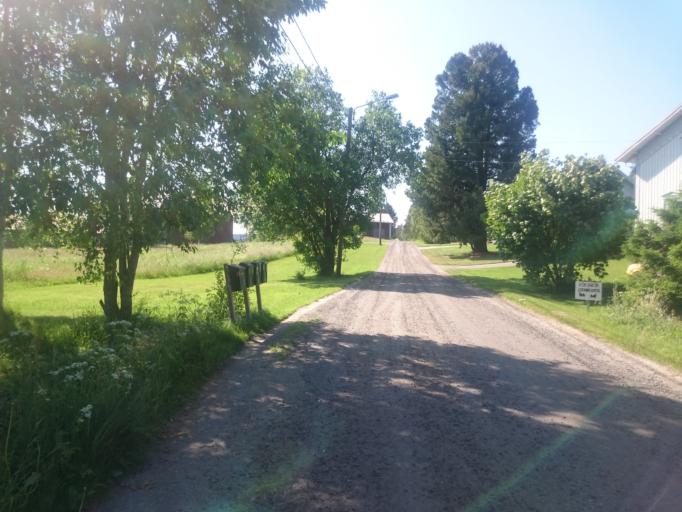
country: SE
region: Vaesternorrland
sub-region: OErnskoeldsviks Kommun
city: Bredbyn
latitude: 63.3000
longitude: 18.2676
